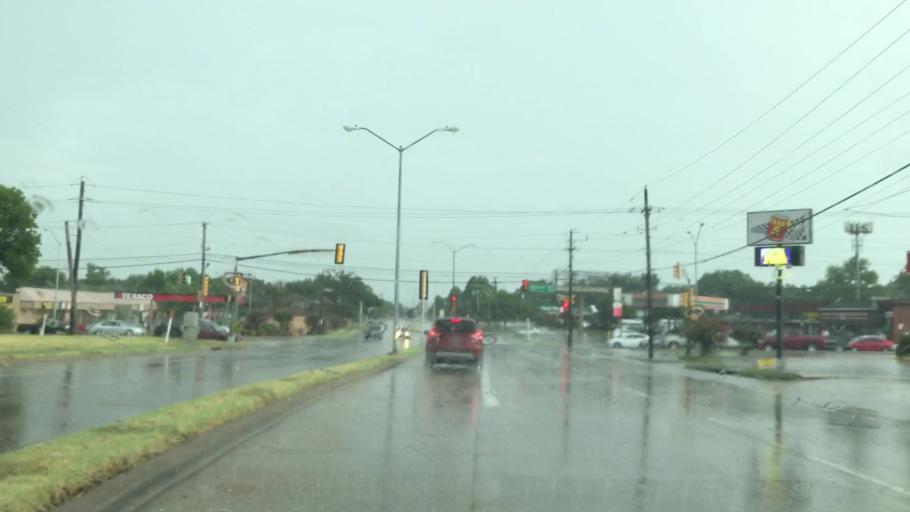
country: US
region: Texas
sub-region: Dallas County
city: Garland
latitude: 32.8796
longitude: -96.7005
